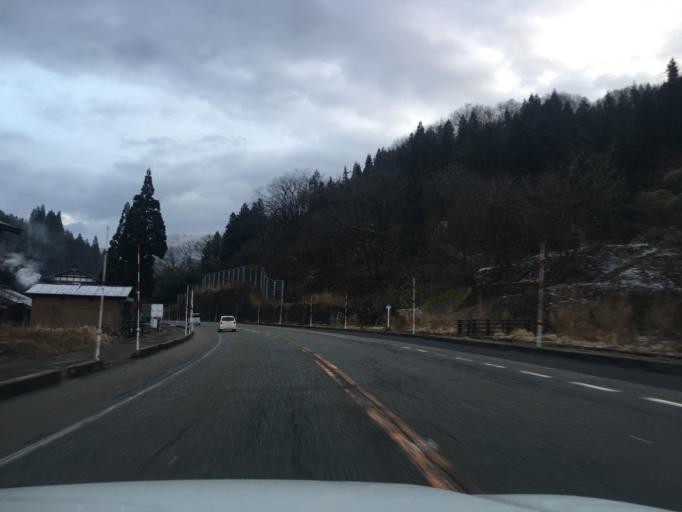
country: JP
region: Niigata
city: Murakami
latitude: 38.3937
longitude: 139.5561
